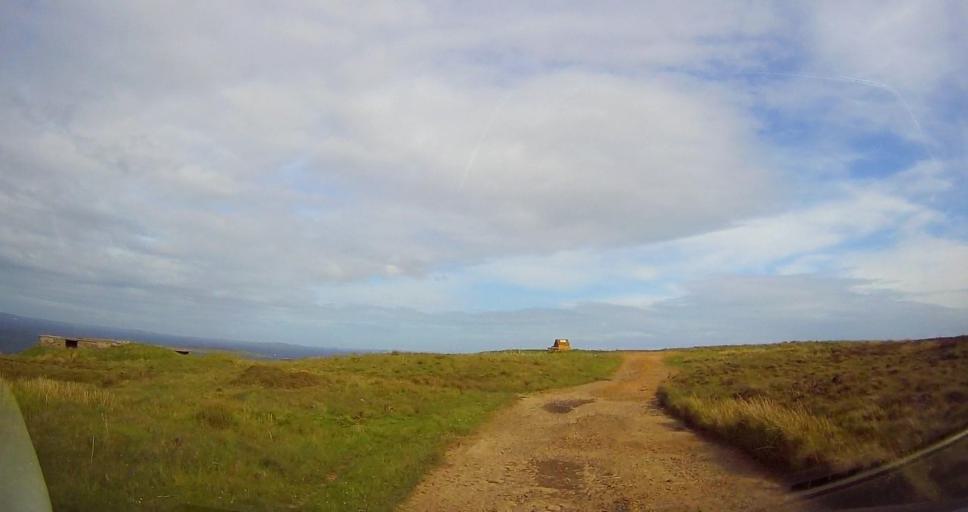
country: GB
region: Scotland
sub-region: Orkney Islands
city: Stromness
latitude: 58.8788
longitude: -3.2427
